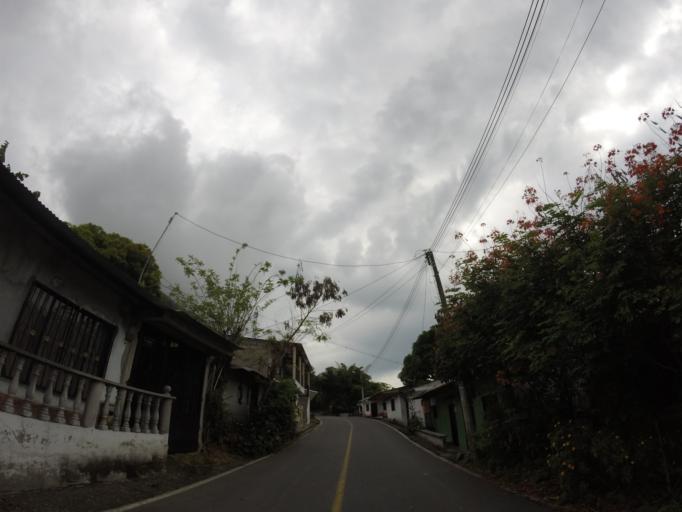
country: CO
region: Caldas
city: Victoria
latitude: 5.3217
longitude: -74.9128
